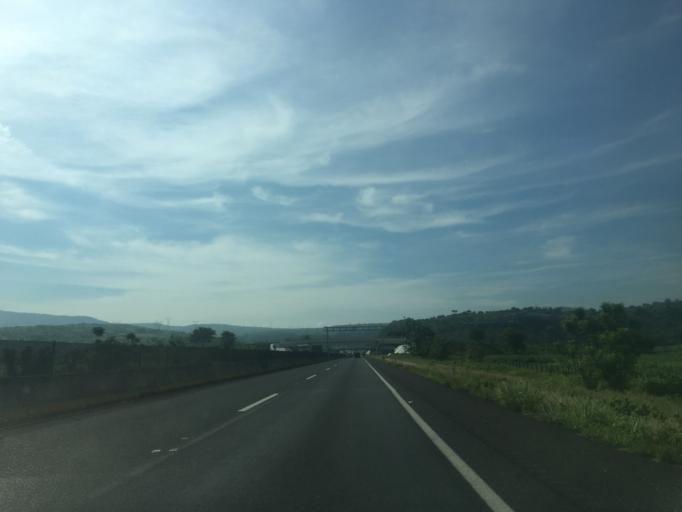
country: MX
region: Nayarit
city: Jala
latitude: 21.0853
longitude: -104.4325
